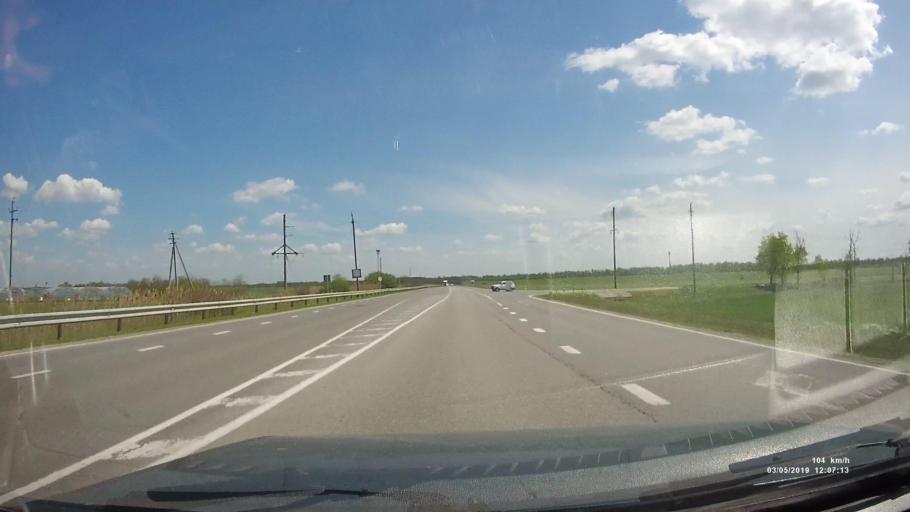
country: RU
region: Rostov
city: Bagayevskaya
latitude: 47.2849
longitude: 40.4701
